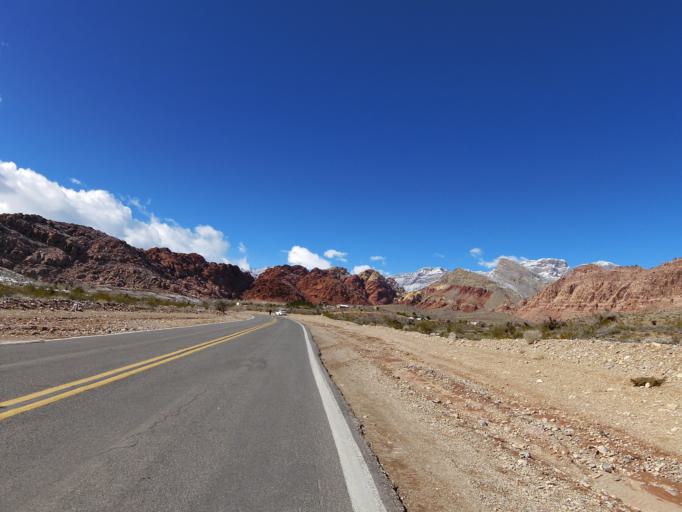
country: US
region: Nevada
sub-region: Clark County
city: Summerlin South
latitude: 36.1468
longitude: -115.4073
